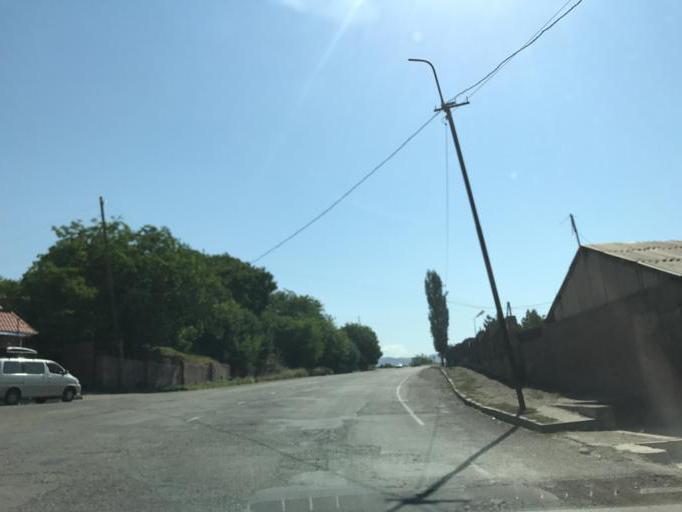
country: AM
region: Vayots' Dzori Marz
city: Yeghegnadzor
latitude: 39.7548
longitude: 45.3363
